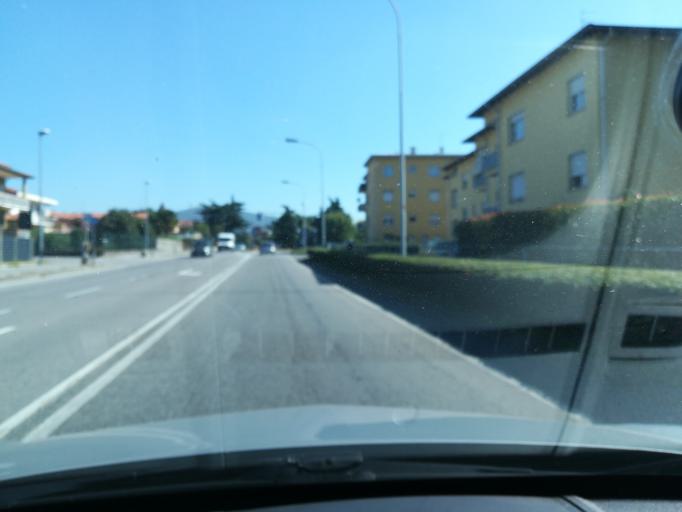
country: IT
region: Lombardy
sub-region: Provincia di Bergamo
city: Montello
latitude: 45.6750
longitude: 9.8044
